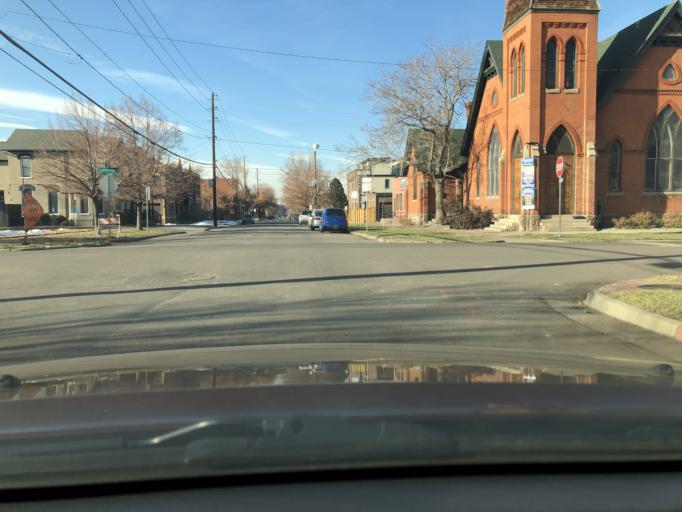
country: US
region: Colorado
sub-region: Denver County
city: Denver
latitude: 39.7535
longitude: -104.9812
